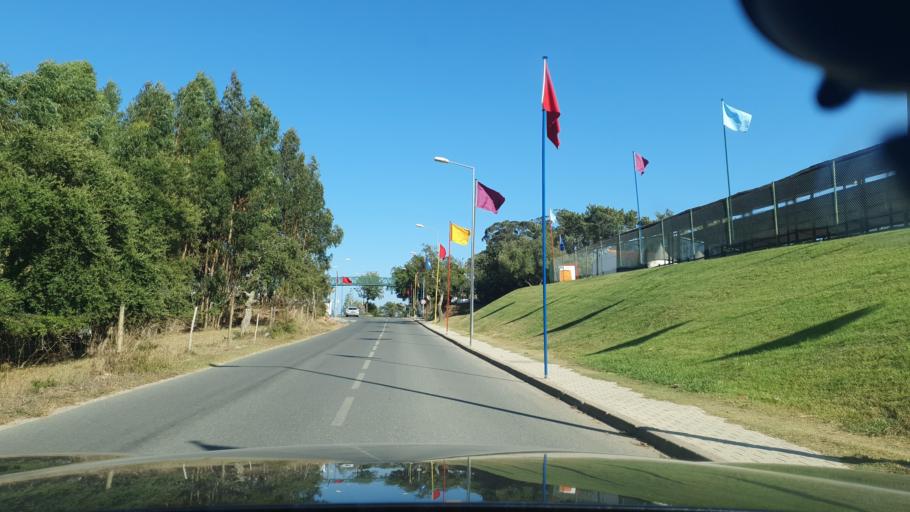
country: PT
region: Beja
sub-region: Odemira
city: Sao Teotonio
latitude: 37.5096
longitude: -8.7116
